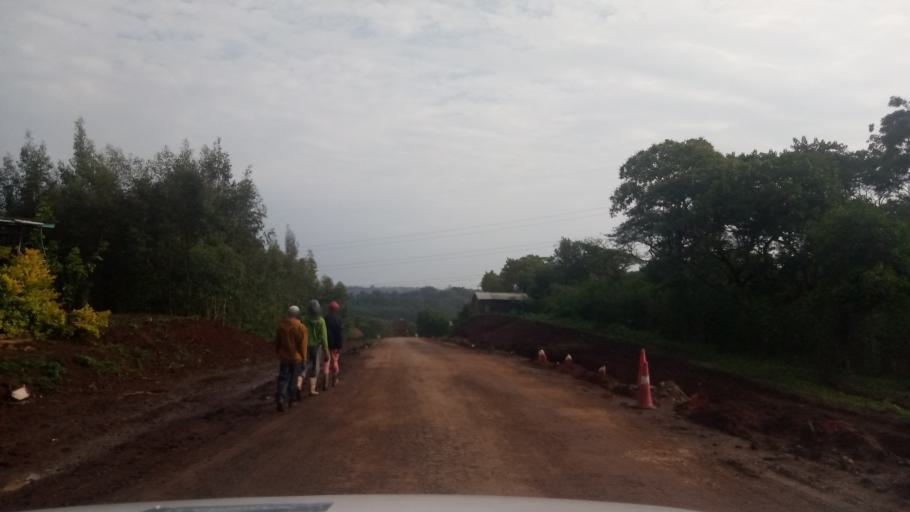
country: ET
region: Oromiya
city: Agaro
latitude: 7.8528
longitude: 36.6547
